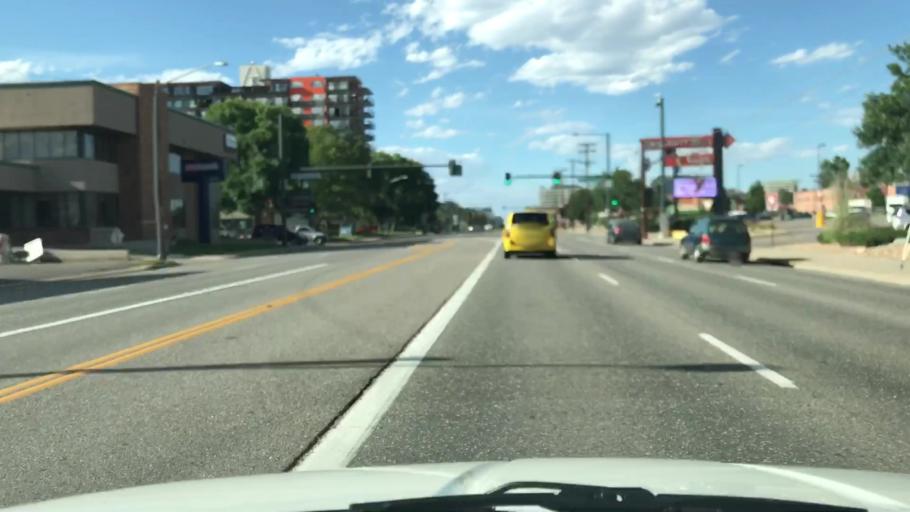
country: US
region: Colorado
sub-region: Arapahoe County
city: Cherry Hills Village
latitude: 39.6697
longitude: -104.9407
